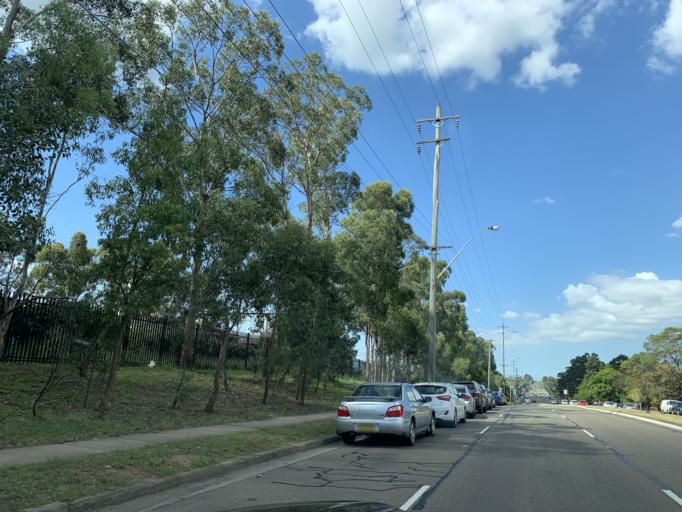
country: AU
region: New South Wales
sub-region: Penrith Municipality
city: Kingswood Park
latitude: -33.7590
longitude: 150.7218
